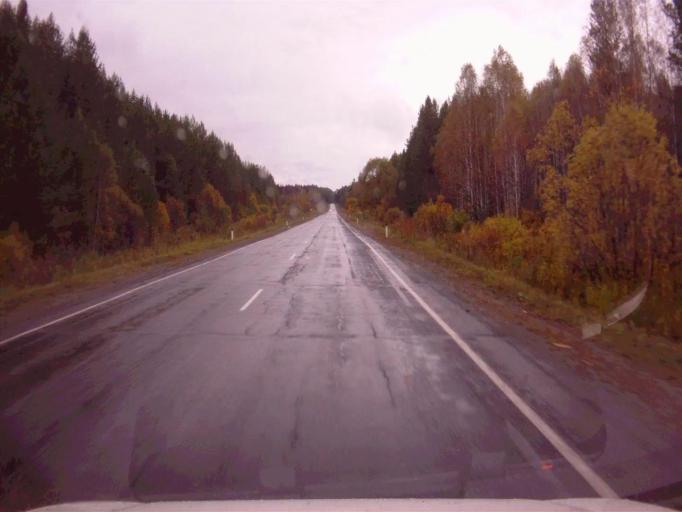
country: RU
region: Chelyabinsk
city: Verkhniy Ufaley
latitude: 56.0146
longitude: 60.3115
